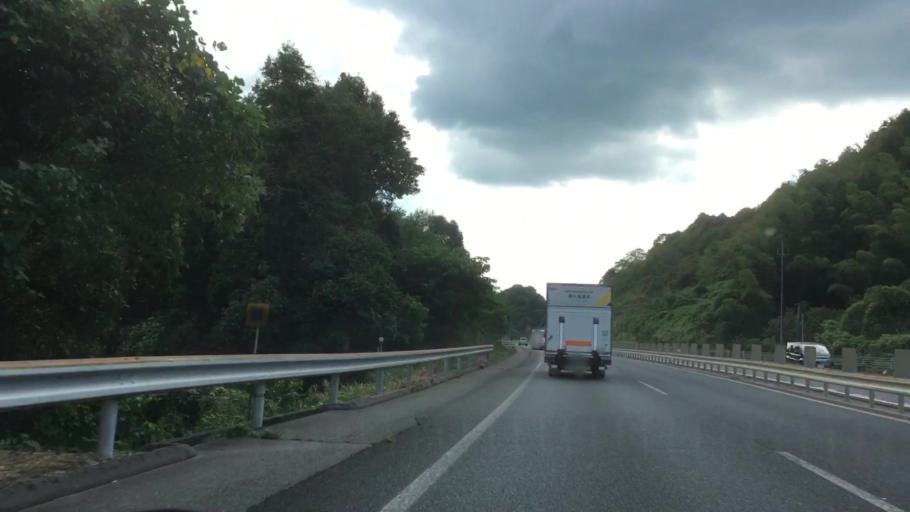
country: JP
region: Yamaguchi
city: Iwakuni
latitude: 34.1314
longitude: 132.1128
